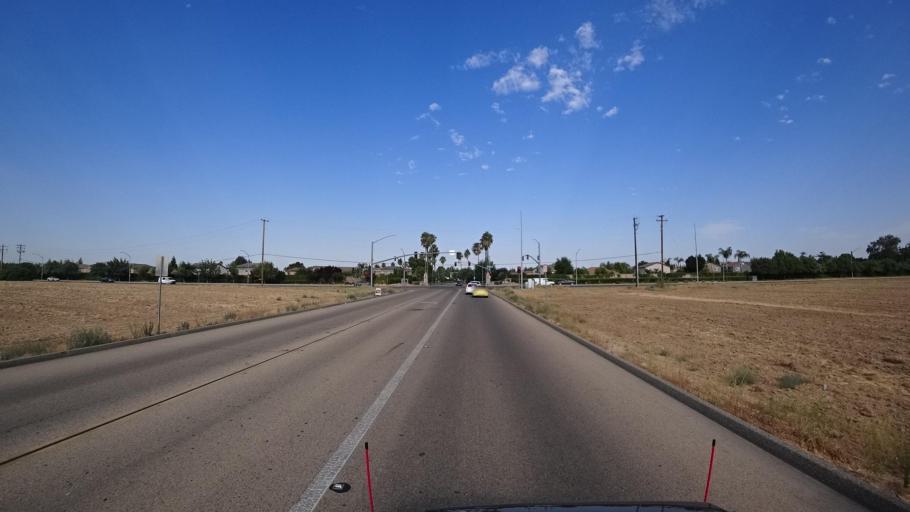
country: US
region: California
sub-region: Fresno County
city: Sunnyside
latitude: 36.7200
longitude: -119.6989
